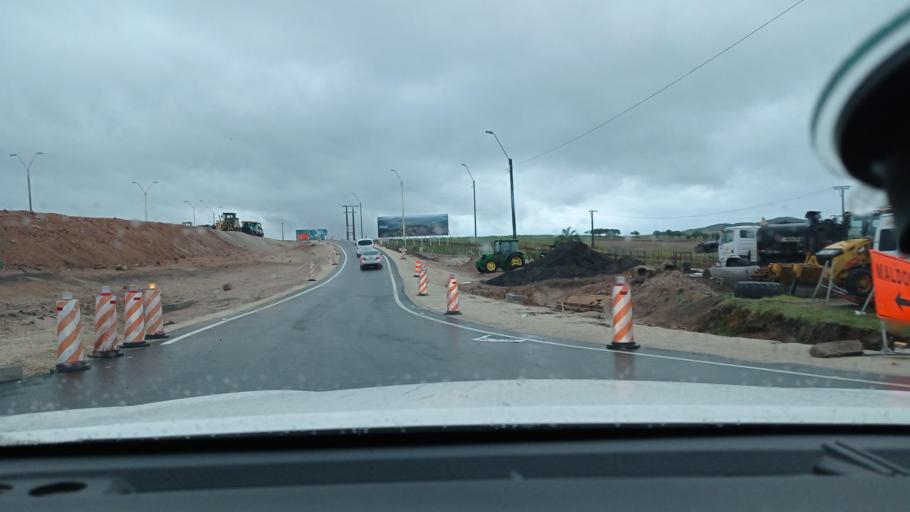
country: UY
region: Maldonado
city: Pan de Azucar
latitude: -34.8327
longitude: -55.2120
